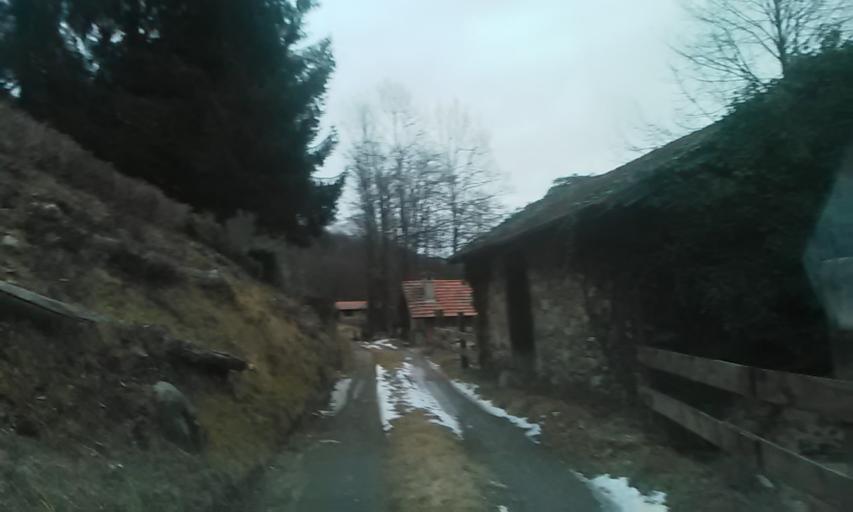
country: IT
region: Piedmont
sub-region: Provincia di Vercelli
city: Quarona
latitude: 45.7825
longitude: 8.2394
